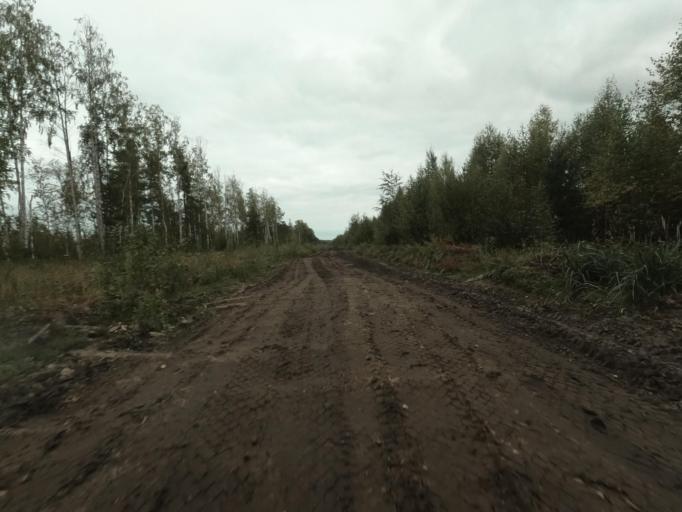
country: RU
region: St.-Petersburg
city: Sapernyy
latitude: 59.7592
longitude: 30.7138
